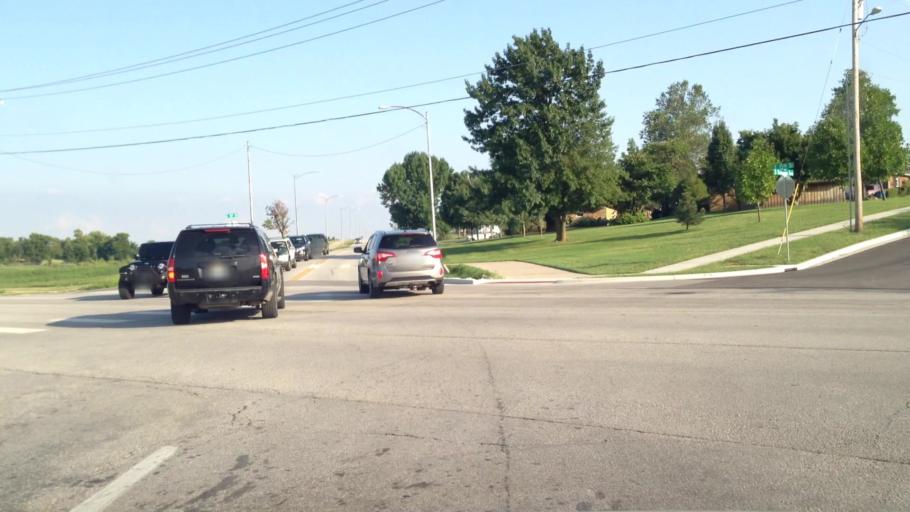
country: US
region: Missouri
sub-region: Jasper County
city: Joplin
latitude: 37.0746
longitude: -94.4910
